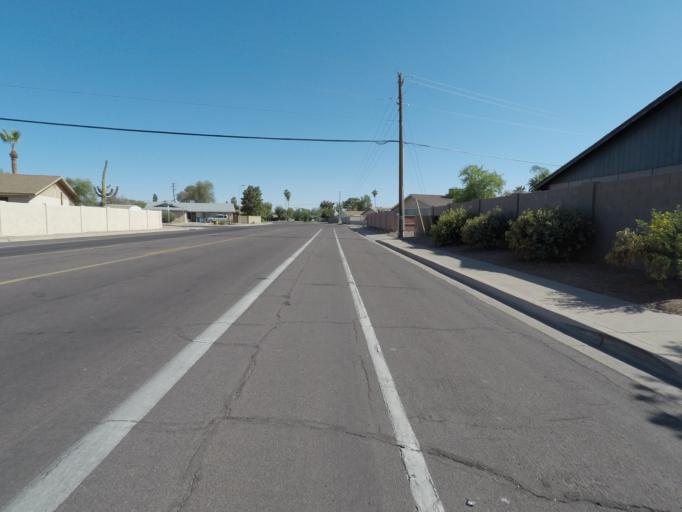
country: US
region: Arizona
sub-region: Maricopa County
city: Tempe
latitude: 33.4052
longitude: -111.9178
